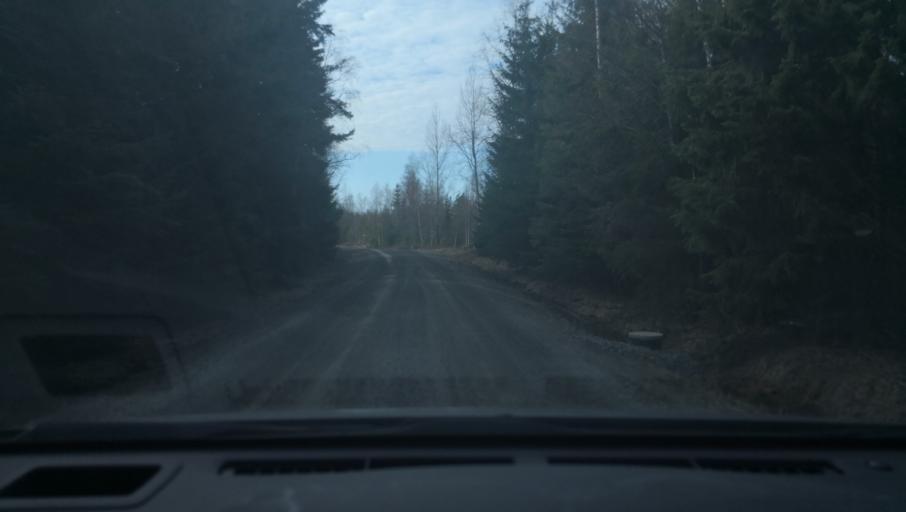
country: SE
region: Uppsala
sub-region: Heby Kommun
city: Heby
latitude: 59.8548
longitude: 16.8667
